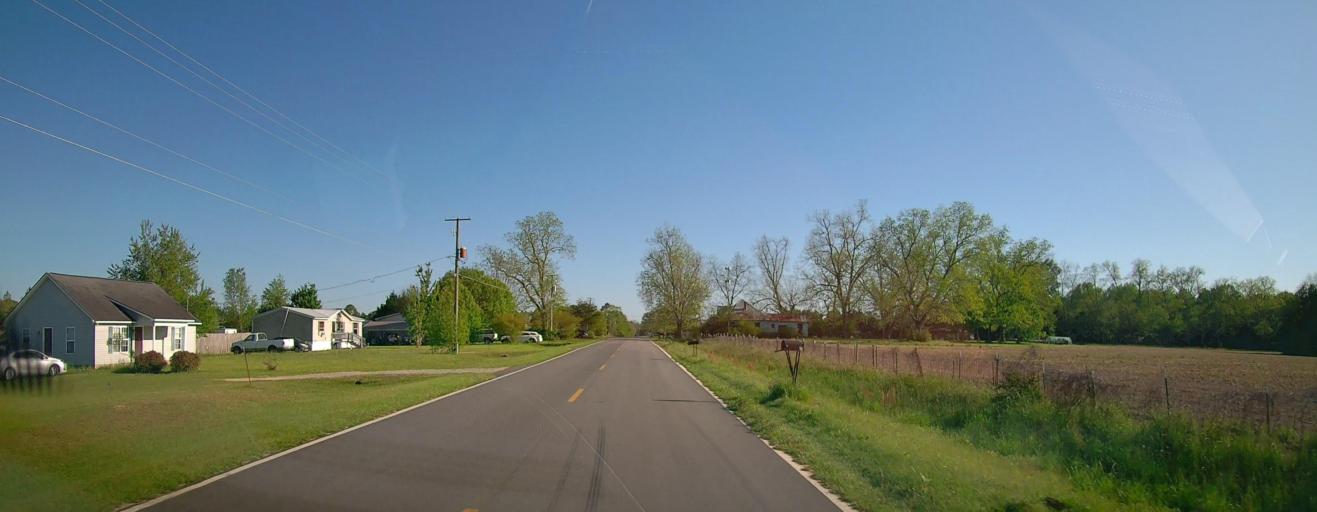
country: US
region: Georgia
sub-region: Ben Hill County
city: Fitzgerald
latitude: 31.7341
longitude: -83.2802
